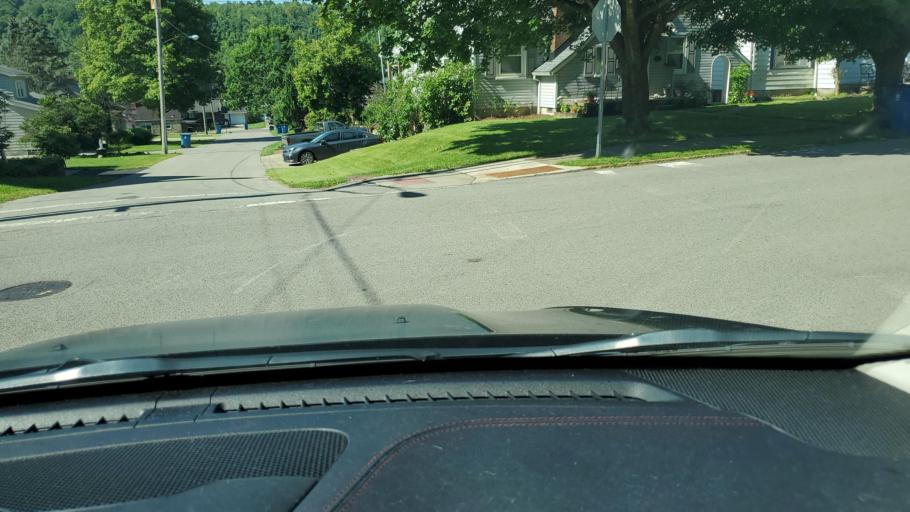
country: US
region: Ohio
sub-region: Mahoning County
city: Lowellville
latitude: 41.0430
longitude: -80.5432
